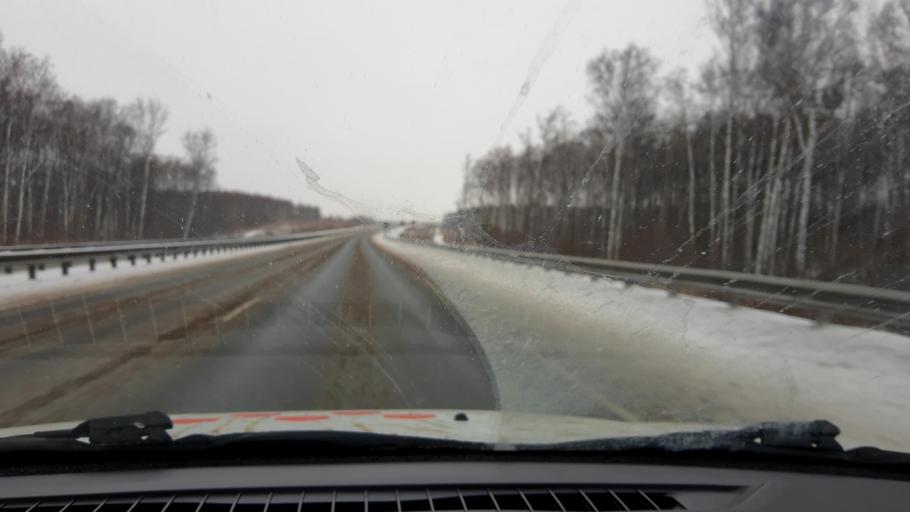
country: RU
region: Nizjnij Novgorod
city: Afonino
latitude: 56.1071
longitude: 43.9884
